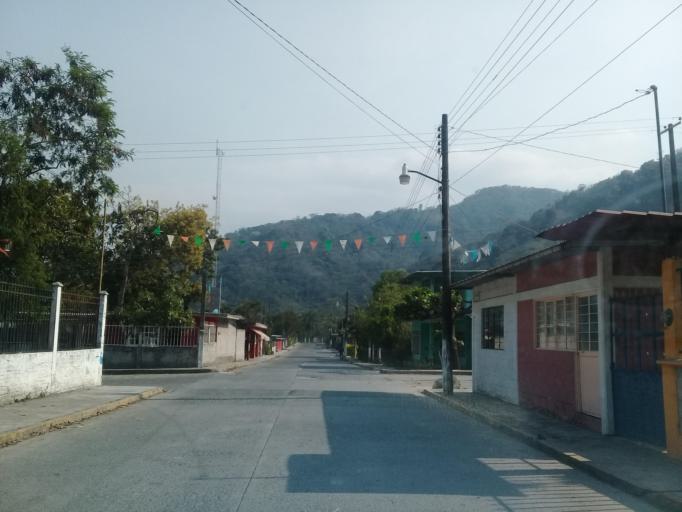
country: MX
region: Veracruz
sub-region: Ixtaczoquitlan
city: Campo Chico
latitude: 18.8366
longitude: -97.0295
